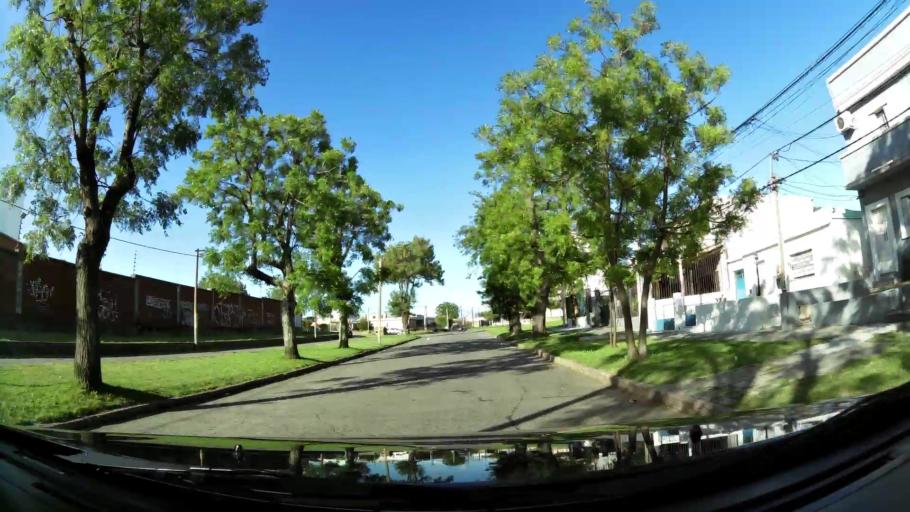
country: UY
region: Montevideo
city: Montevideo
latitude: -34.8748
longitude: -56.1509
